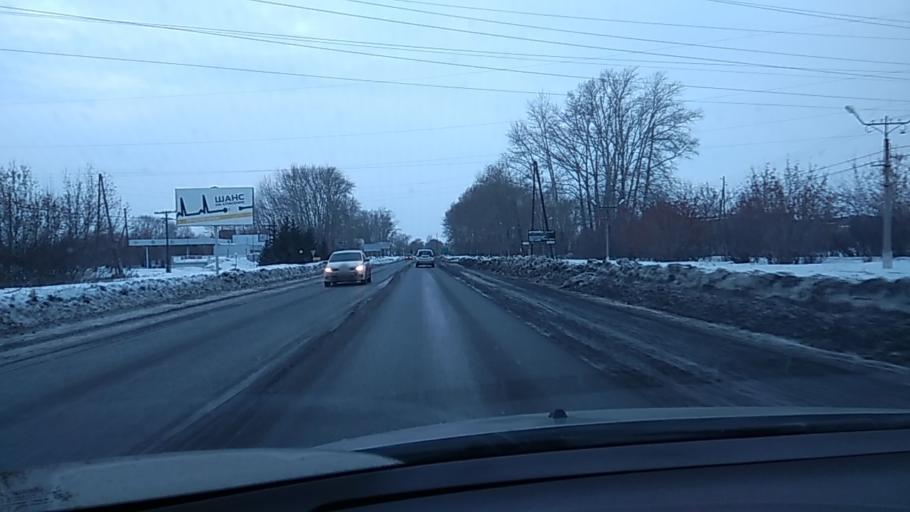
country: RU
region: Sverdlovsk
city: Martyush
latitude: 56.4432
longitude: 61.8259
